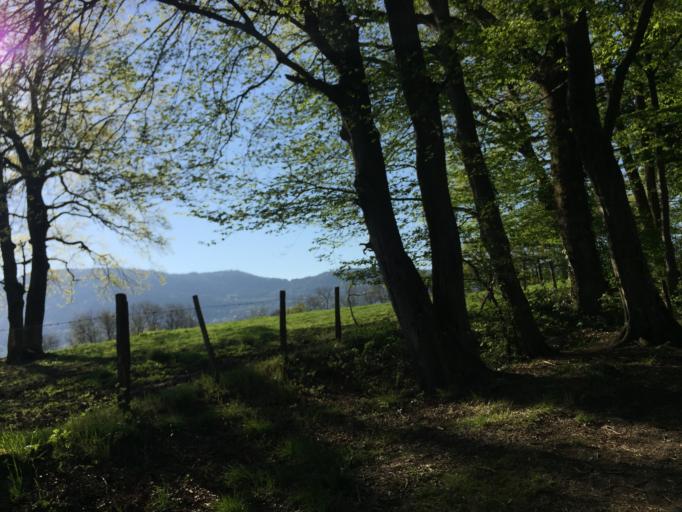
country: FR
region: Rhone-Alpes
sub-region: Departement de la Savoie
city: Challes-les-Eaux
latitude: 45.5306
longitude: 5.9761
